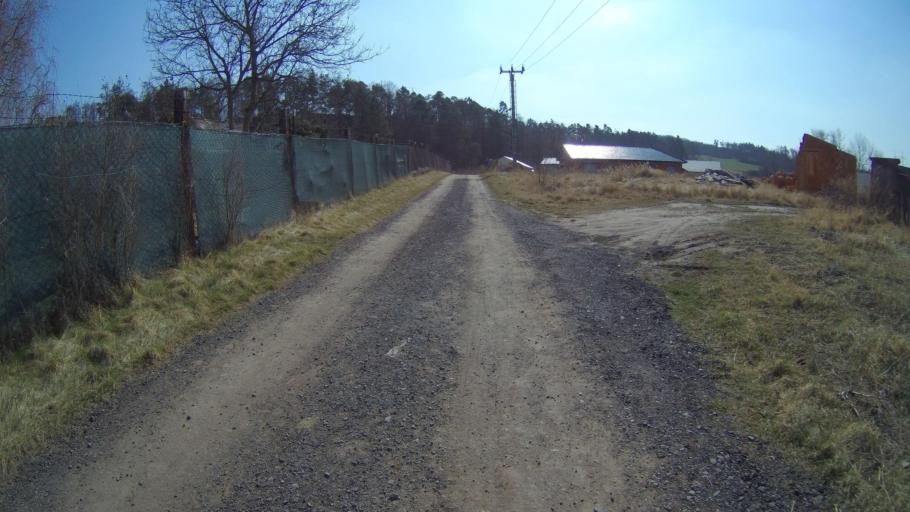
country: CZ
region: Ustecky
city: Mecholupy
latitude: 50.2728
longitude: 13.5665
